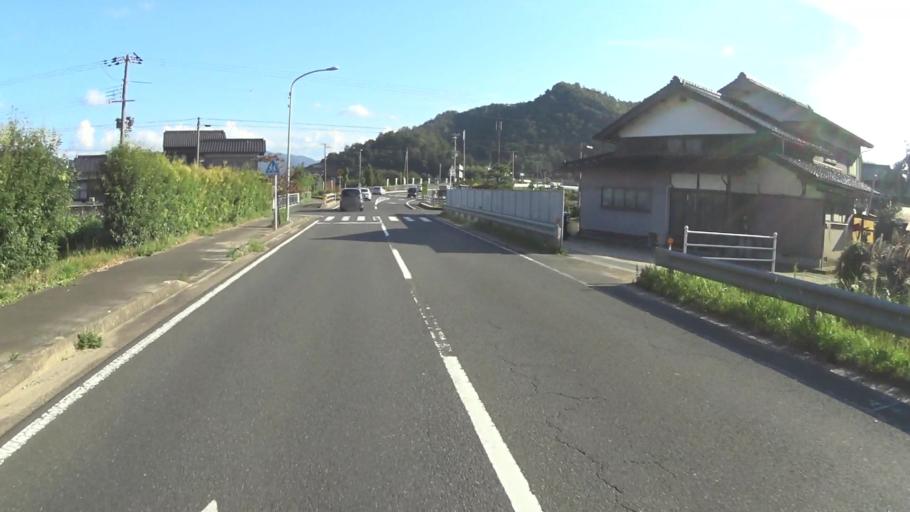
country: JP
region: Hyogo
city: Toyooka
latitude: 35.6108
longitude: 134.9192
